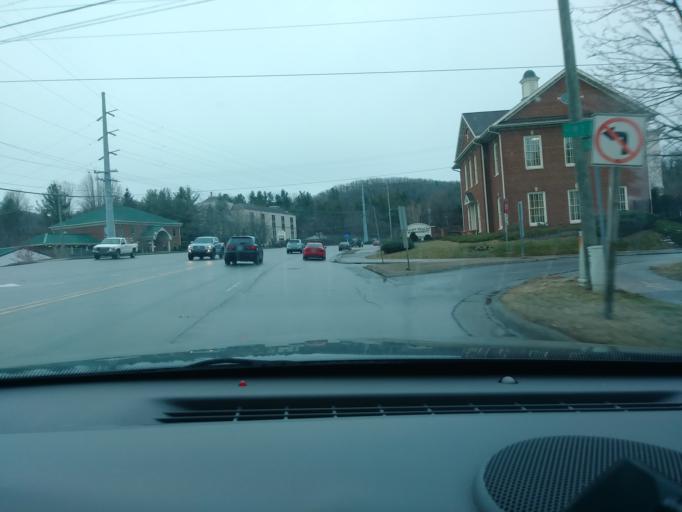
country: US
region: North Carolina
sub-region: Watauga County
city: Boone
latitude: 36.2051
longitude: -81.6703
